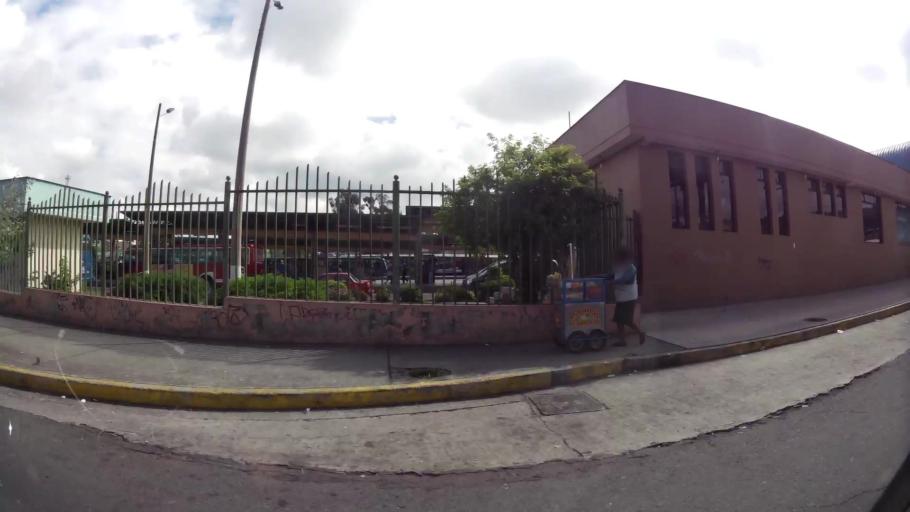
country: EC
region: Pichincha
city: Quito
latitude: -0.1637
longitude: -78.4731
